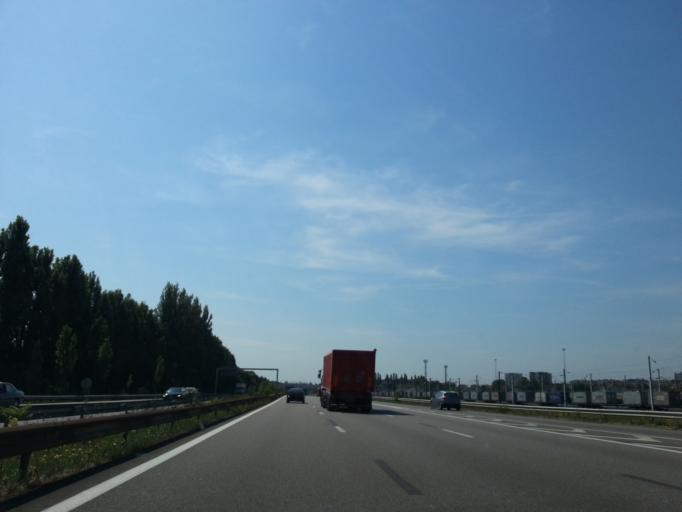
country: FR
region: Alsace
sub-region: Departement du Bas-Rhin
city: Schiltigheim
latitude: 48.6130
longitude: 7.7266
